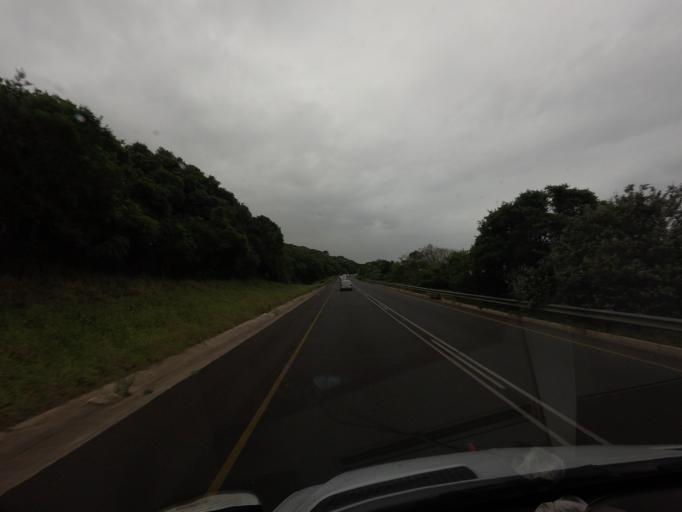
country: ZA
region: KwaZulu-Natal
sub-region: eThekwini Metropolitan Municipality
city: Durban
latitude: -29.7122
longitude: 31.0913
